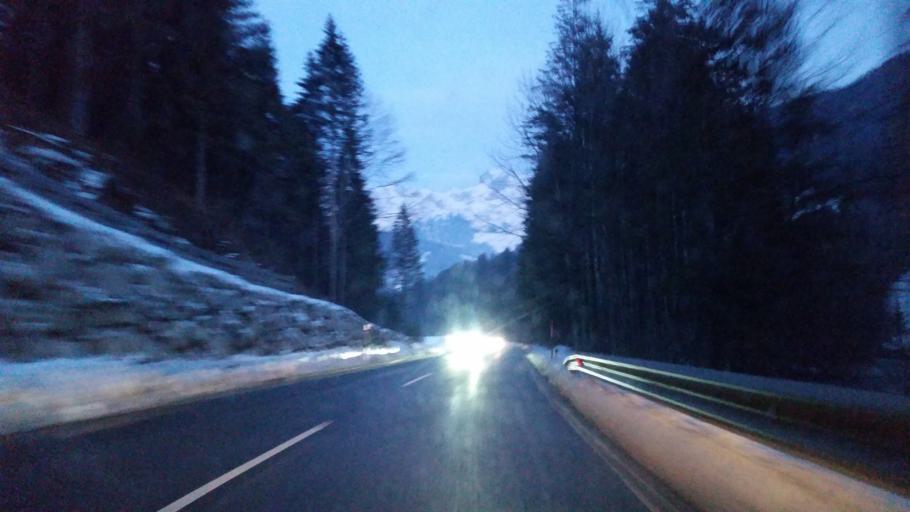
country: AT
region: Salzburg
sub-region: Politischer Bezirk Hallein
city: Abtenau
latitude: 47.5000
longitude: 13.4144
